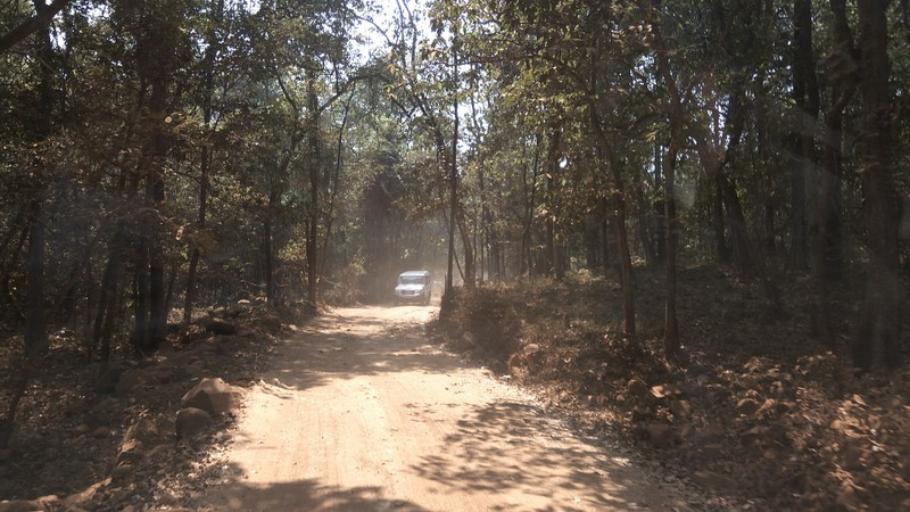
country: IN
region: Goa
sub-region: South Goa
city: Sanguem
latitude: 15.3258
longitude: 74.2838
